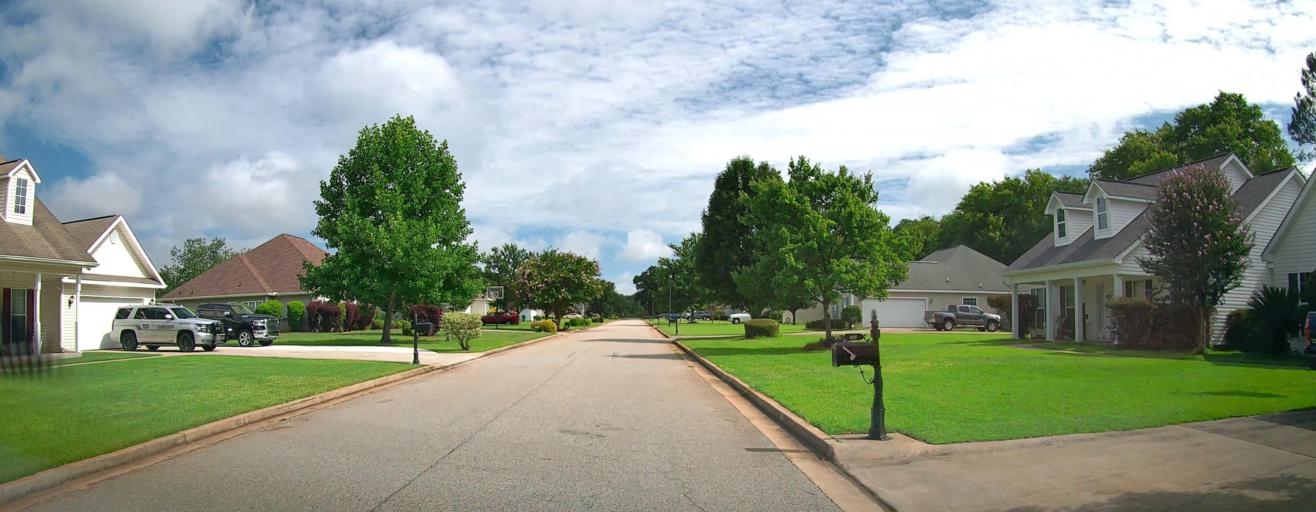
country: US
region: Georgia
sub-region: Peach County
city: Byron
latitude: 32.6475
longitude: -83.7245
